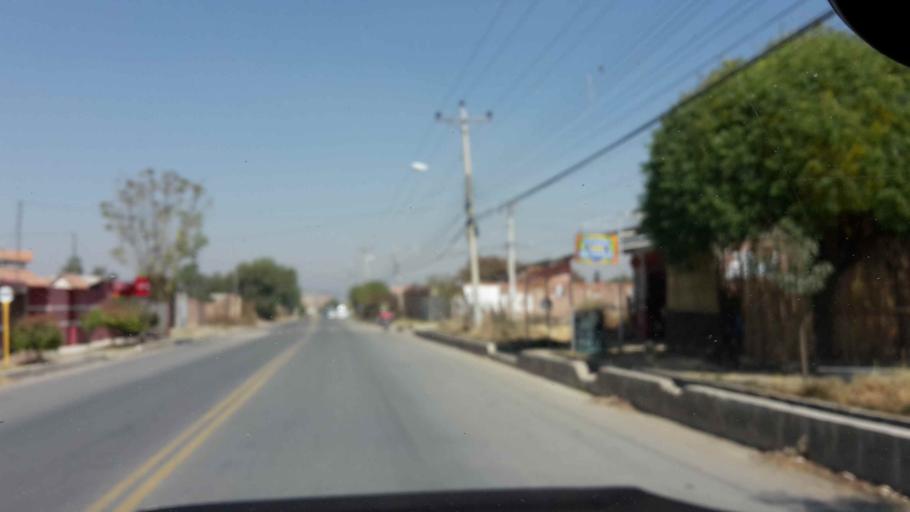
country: BO
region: Cochabamba
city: Cochabamba
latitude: -17.3663
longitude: -66.2308
